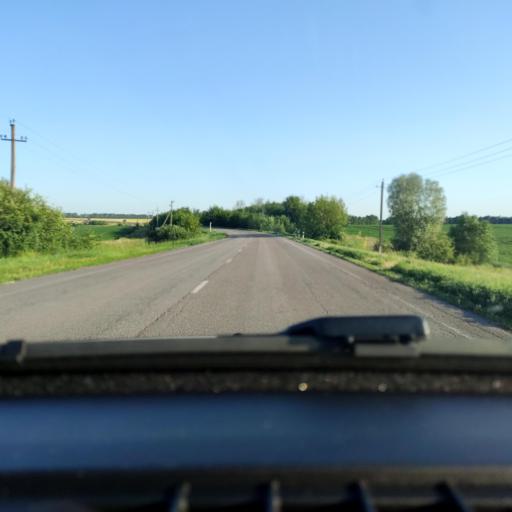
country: RU
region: Voronezj
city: Kashirskoye
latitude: 51.5056
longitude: 39.8322
